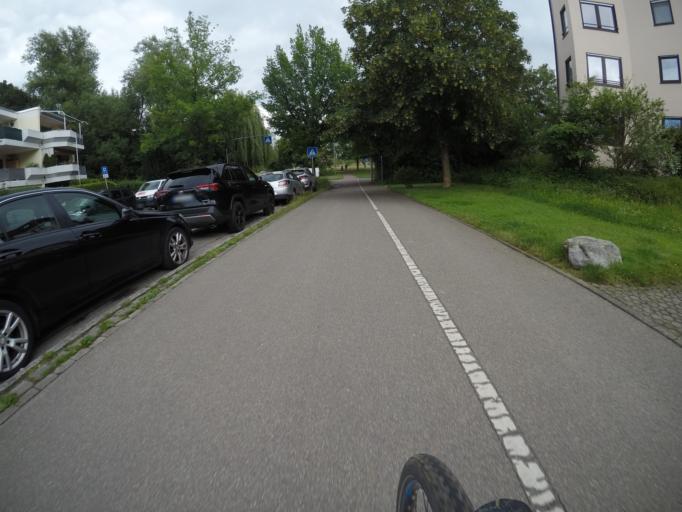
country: DE
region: Baden-Wuerttemberg
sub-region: Regierungsbezirk Stuttgart
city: Filderstadt
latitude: 48.6725
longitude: 9.2176
